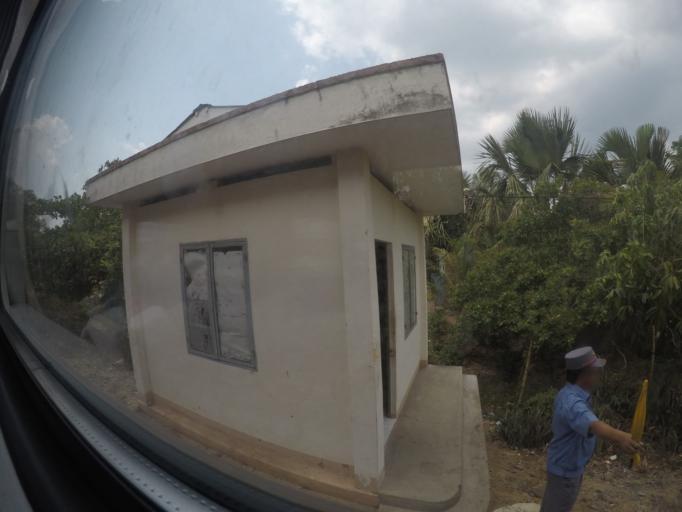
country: VN
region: Binh Thuan
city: Tanh Linh
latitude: 10.9700
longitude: 107.6285
